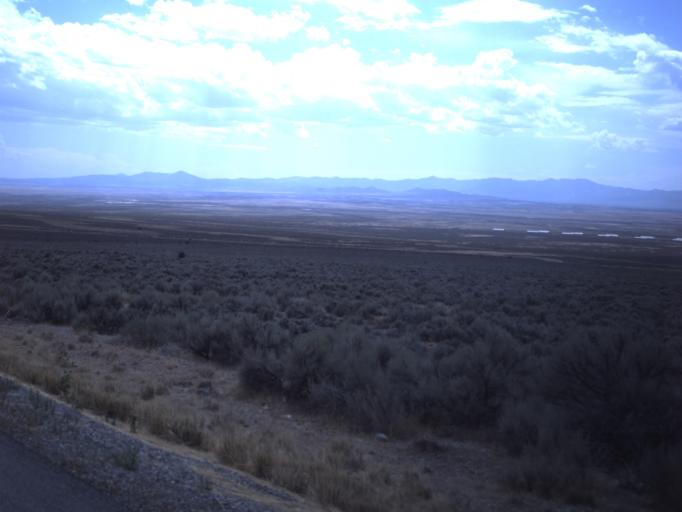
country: US
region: Utah
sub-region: Tooele County
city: Tooele
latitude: 40.3132
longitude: -112.2827
